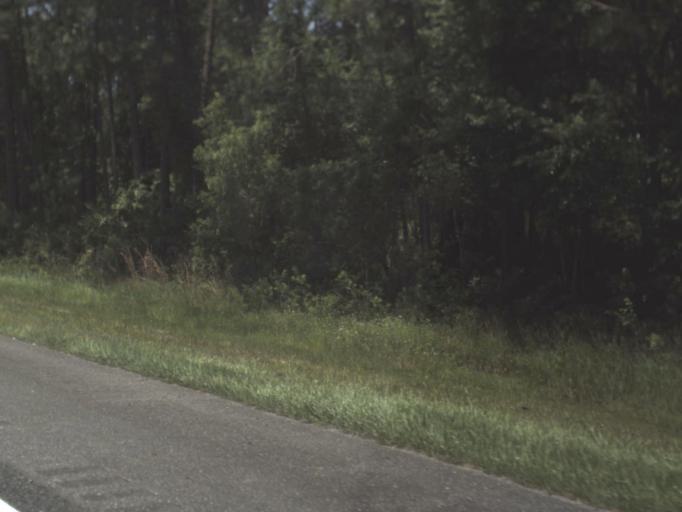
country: US
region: Florida
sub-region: Columbia County
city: Watertown
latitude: 30.2551
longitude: -82.4374
